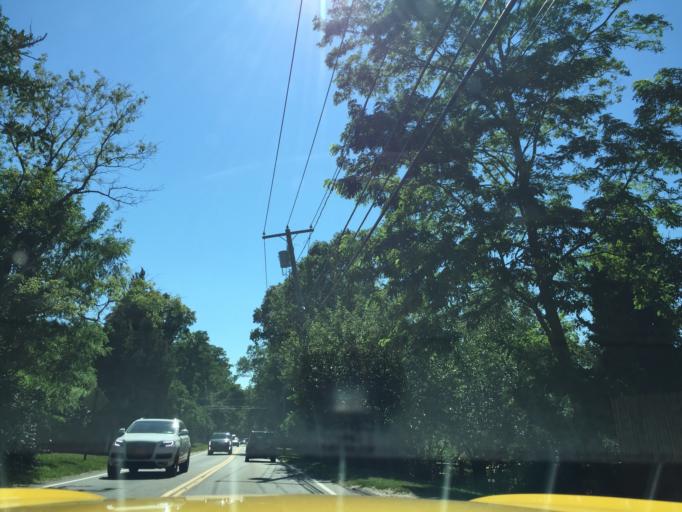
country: US
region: New York
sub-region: Suffolk County
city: Noyack
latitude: 40.9889
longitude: -72.3624
